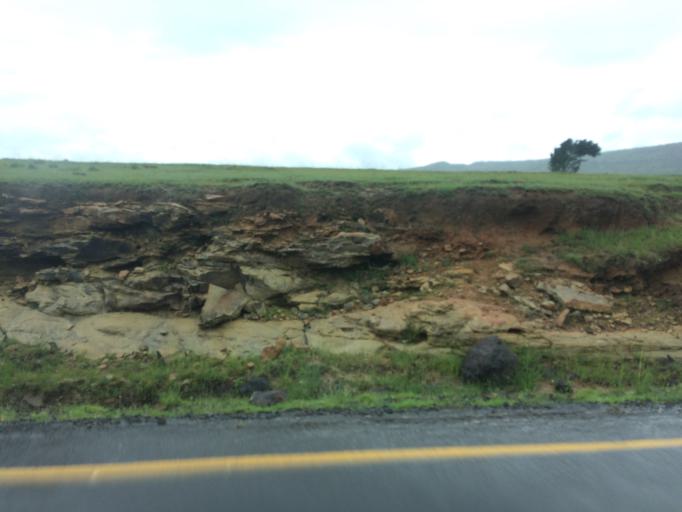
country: LS
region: Mafeteng
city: Mafeteng
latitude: -29.7356
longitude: 27.5041
